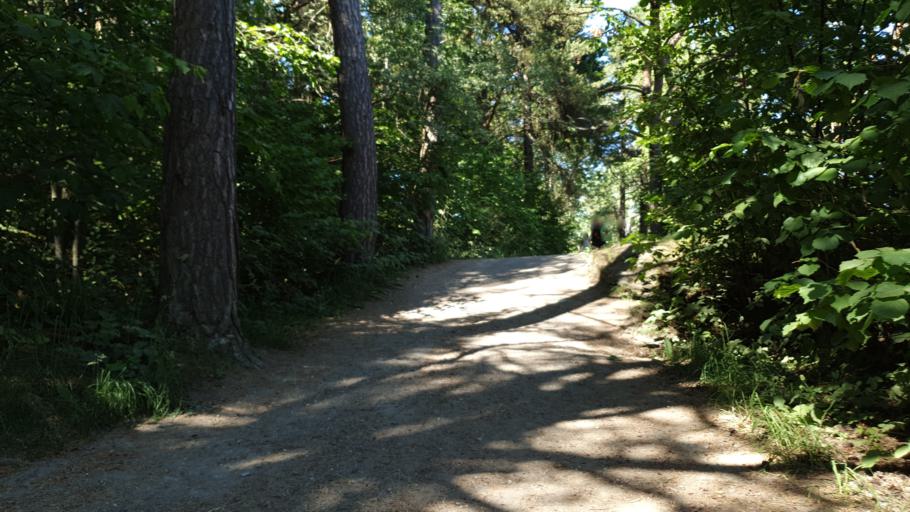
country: NO
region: Sor-Trondelag
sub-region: Trondheim
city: Trondheim
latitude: 63.4466
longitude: 10.4677
